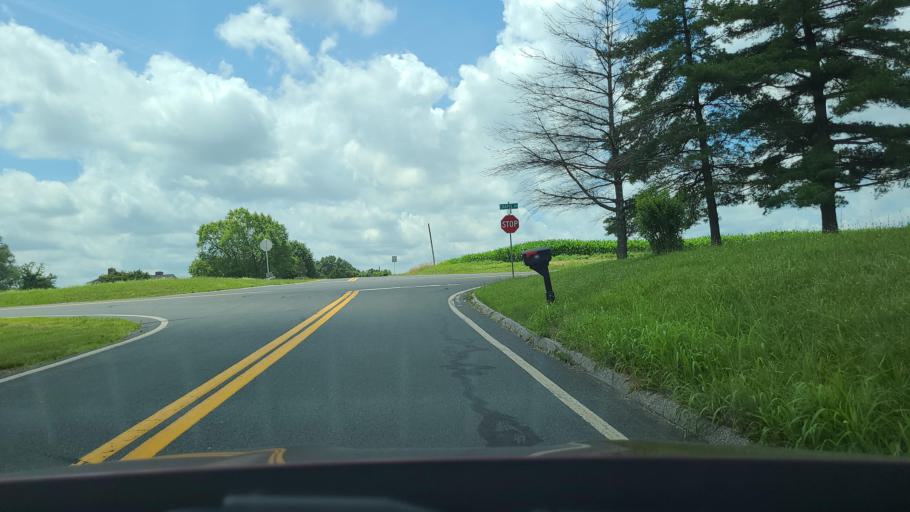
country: US
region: Maryland
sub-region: Carroll County
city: Westminster
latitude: 39.5414
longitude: -77.0274
